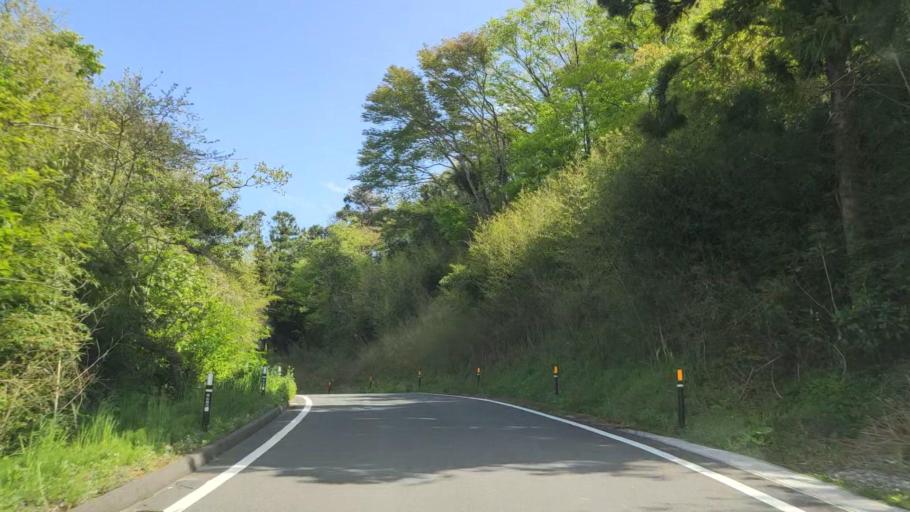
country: JP
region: Miyagi
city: Matsushima
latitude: 38.3383
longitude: 141.1577
